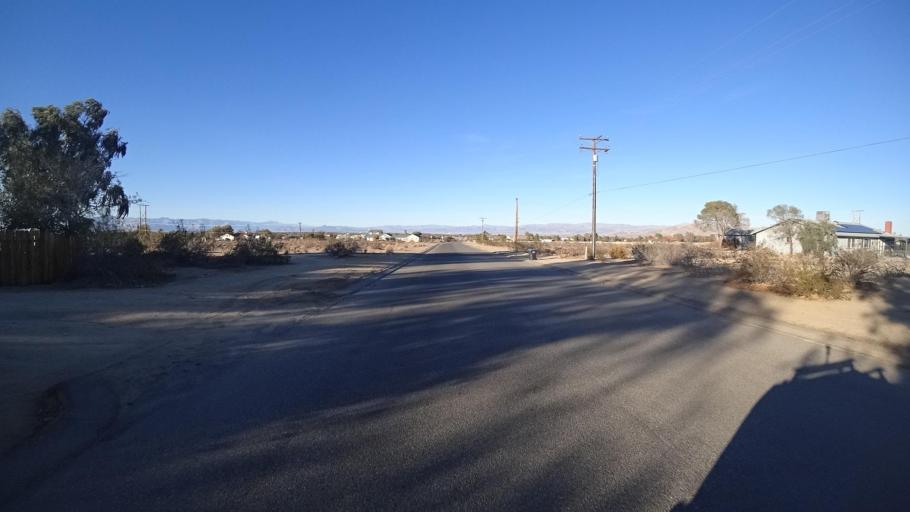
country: US
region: California
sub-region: Kern County
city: Ridgecrest
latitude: 35.5919
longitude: -117.6617
